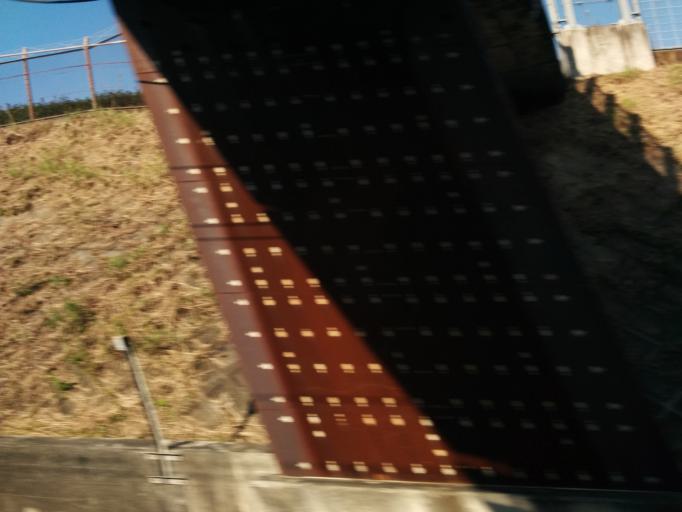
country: JP
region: Shizuoka
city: Kakegawa
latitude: 34.7714
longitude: 138.0644
